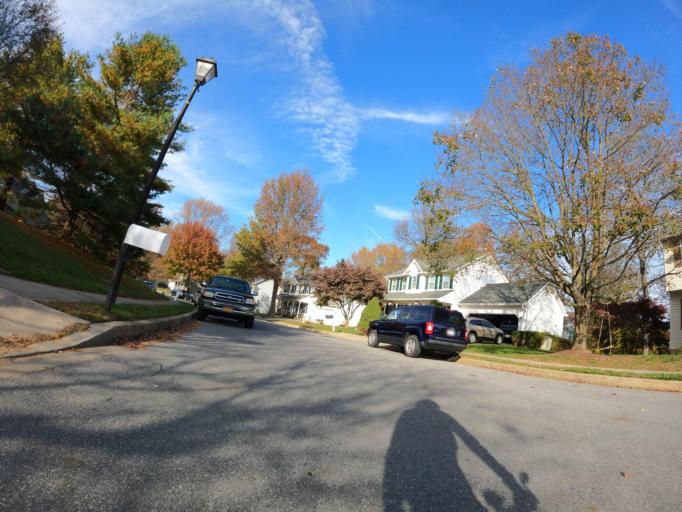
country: US
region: Maryland
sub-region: Carroll County
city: Sykesville
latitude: 39.3653
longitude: -76.9727
